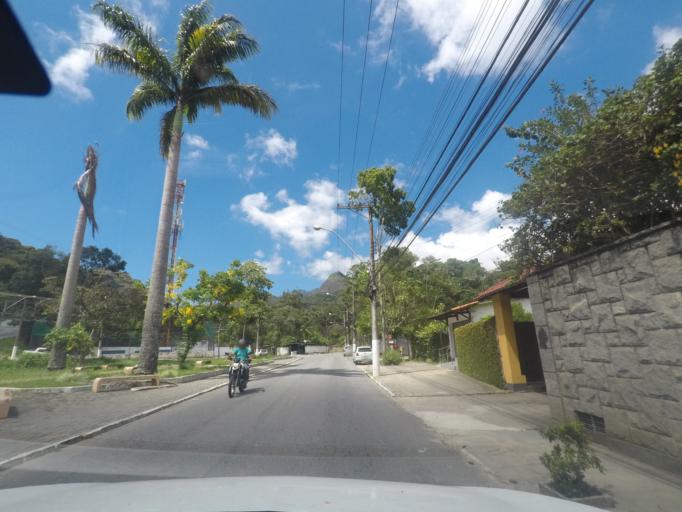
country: BR
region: Rio de Janeiro
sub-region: Teresopolis
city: Teresopolis
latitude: -22.4108
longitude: -42.9806
